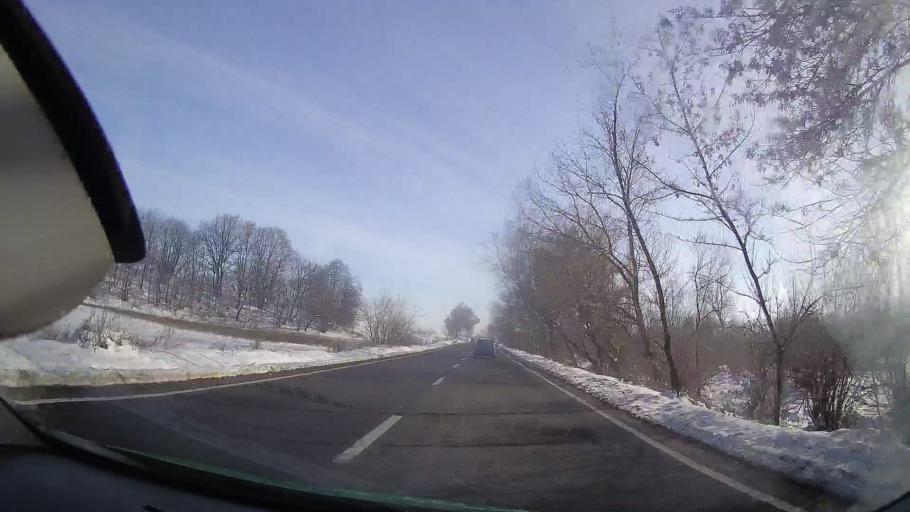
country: RO
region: Neamt
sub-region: Comuna Negresti
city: Negresti
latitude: 47.0694
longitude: 26.3672
